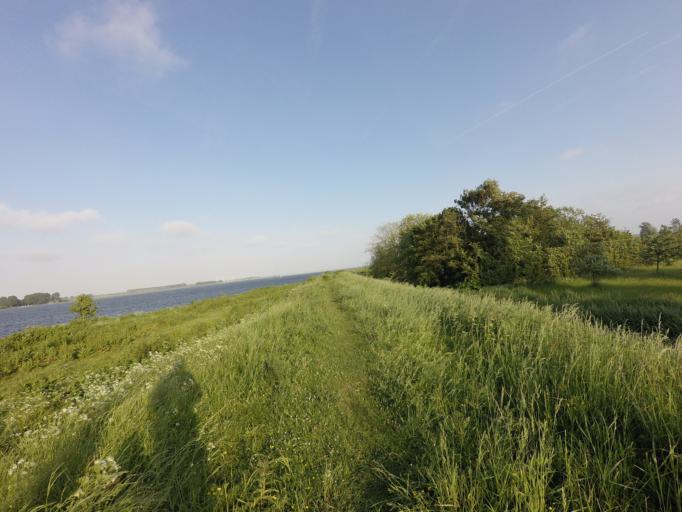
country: NL
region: North Brabant
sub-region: Gemeente Moerdijk
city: Willemstad
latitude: 51.7355
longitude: 4.3553
